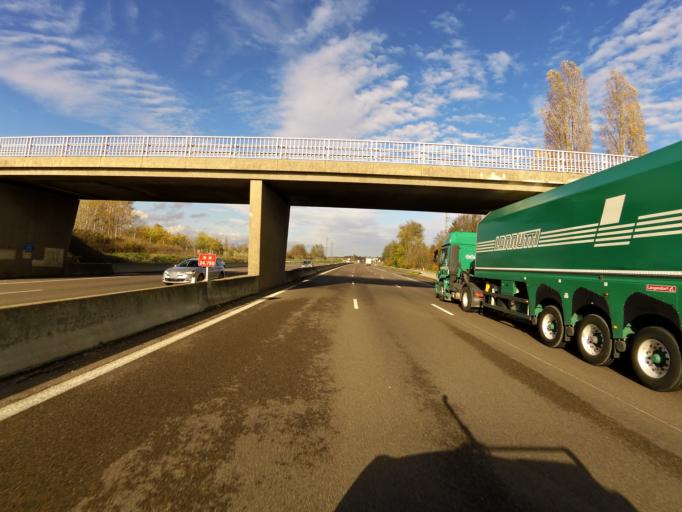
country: FR
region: Bourgogne
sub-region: Departement de la Cote-d'Or
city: Gevrey-Chambertin
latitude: 47.2105
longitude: 4.9995
